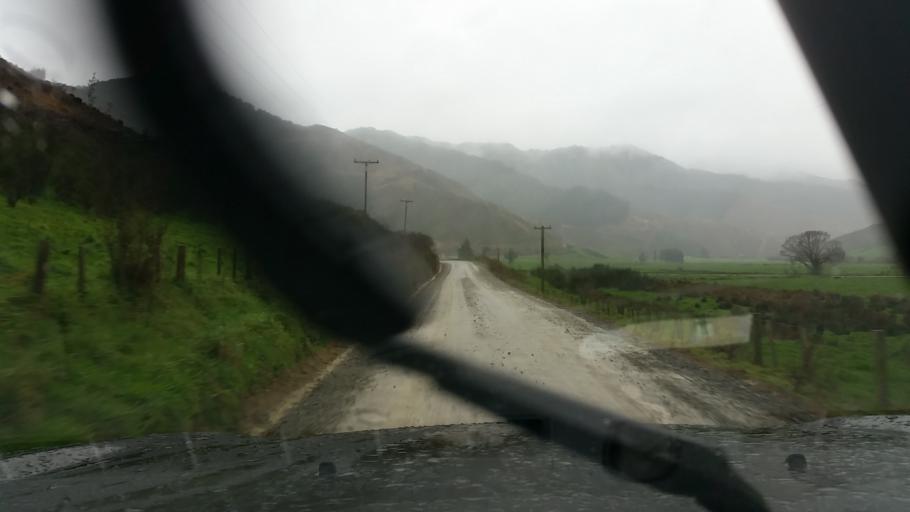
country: NZ
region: Marlborough
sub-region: Marlborough District
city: Picton
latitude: -41.3465
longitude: 173.9291
